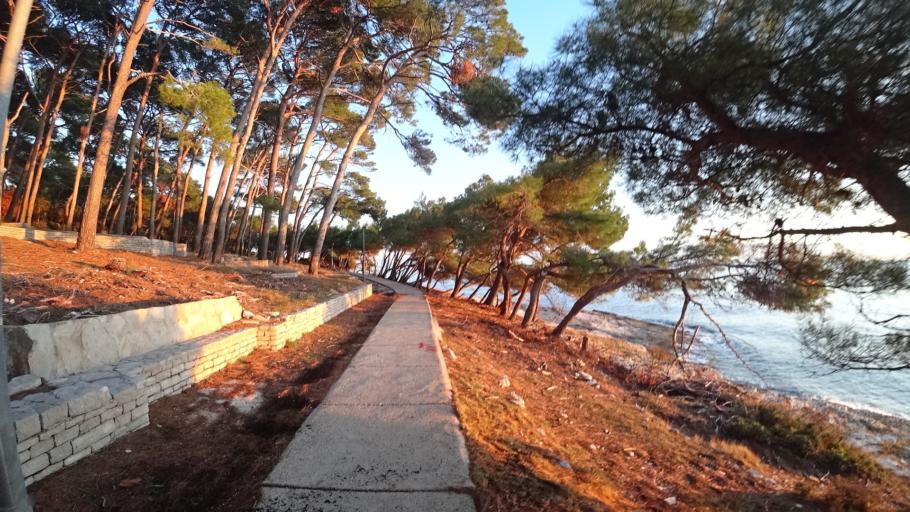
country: HR
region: Primorsko-Goranska
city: Mali Losinj
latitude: 44.5251
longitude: 14.4488
